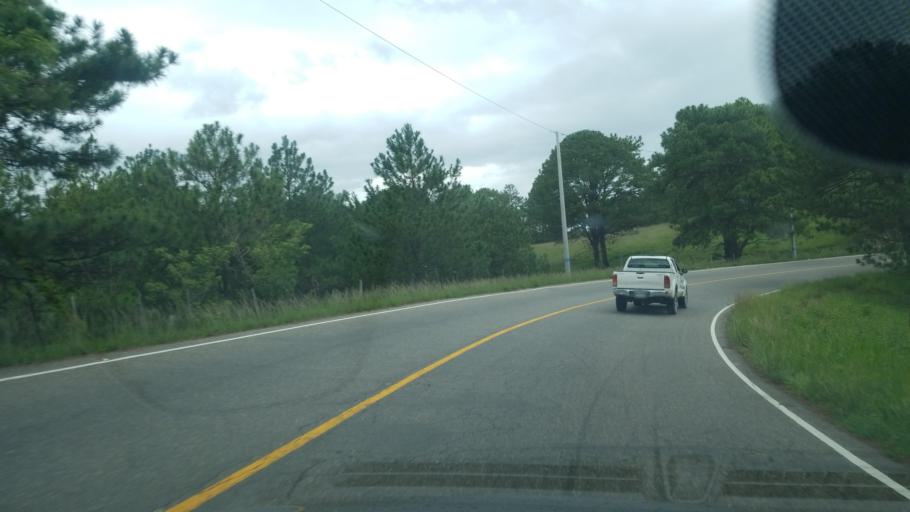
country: HN
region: Ocotepeque
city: Sinuapa
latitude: 14.4599
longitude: -89.1603
